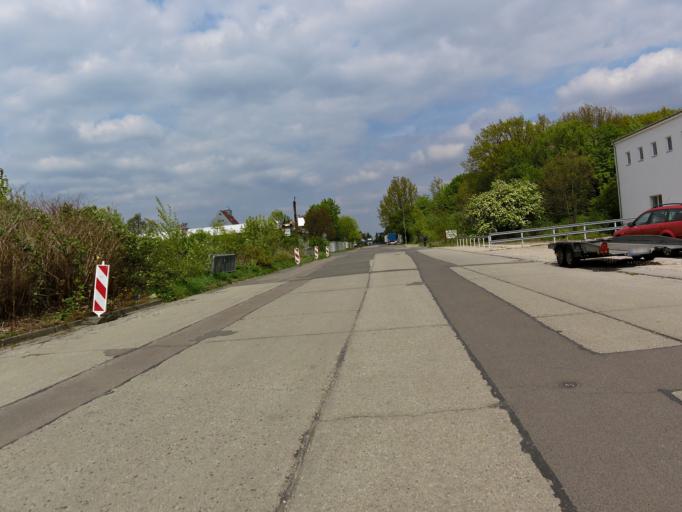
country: DE
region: Saxony
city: Leipzig
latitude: 51.3733
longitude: 12.3960
